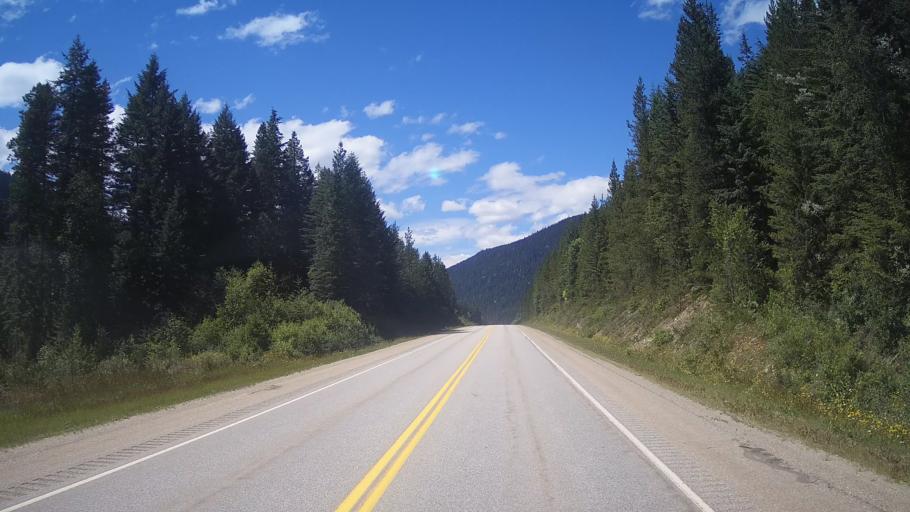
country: CA
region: Alberta
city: Grande Cache
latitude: 53.0145
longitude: -119.0774
